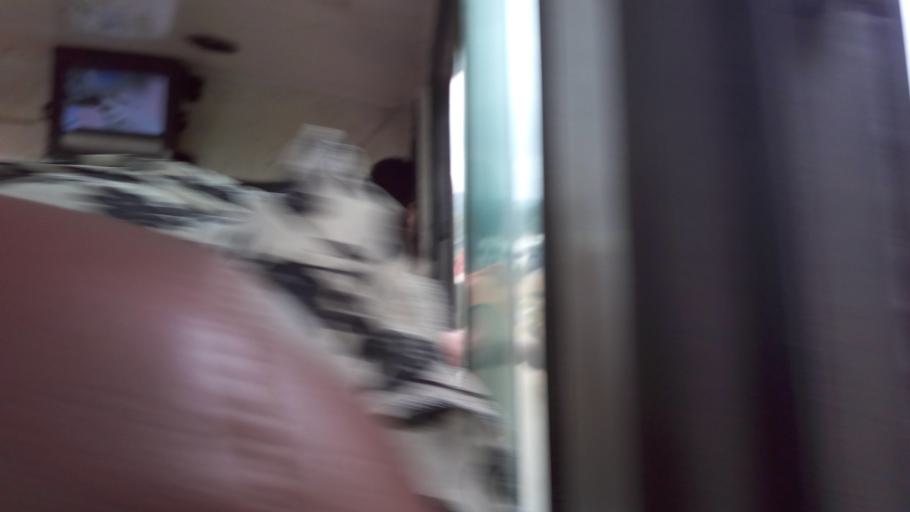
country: CI
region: Lagunes
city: Abidjan
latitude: 5.3382
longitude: -4.1213
